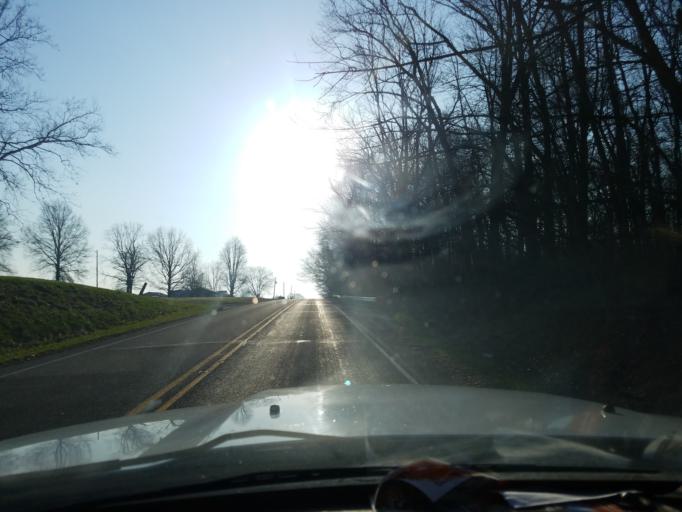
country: US
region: Indiana
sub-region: Clay County
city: Middlebury
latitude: 39.3880
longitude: -87.1653
